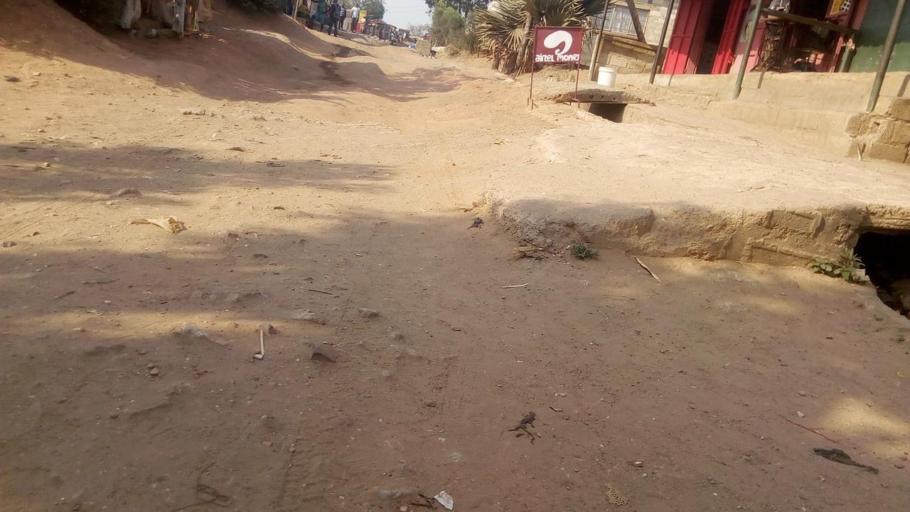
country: ZM
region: Lusaka
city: Lusaka
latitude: -15.3587
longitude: 28.2981
